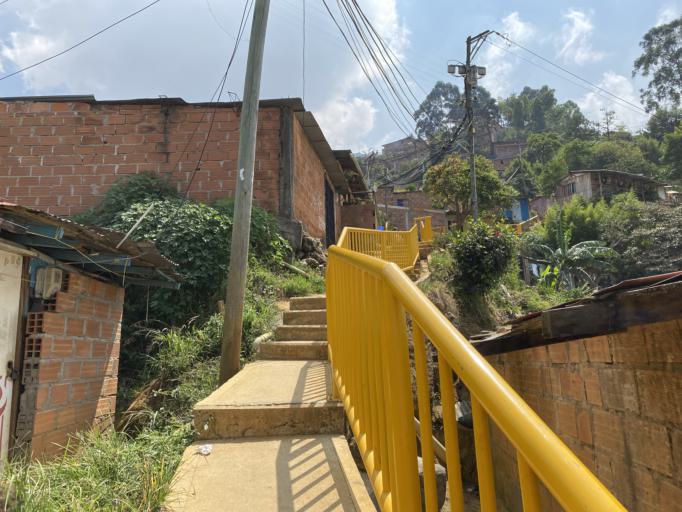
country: CO
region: Antioquia
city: Medellin
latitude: 6.2676
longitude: -75.5414
